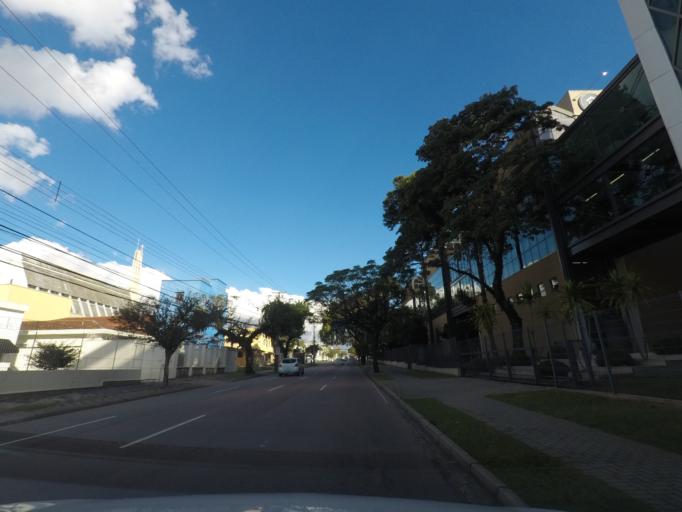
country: BR
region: Parana
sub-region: Curitiba
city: Curitiba
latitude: -25.4491
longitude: -49.2653
